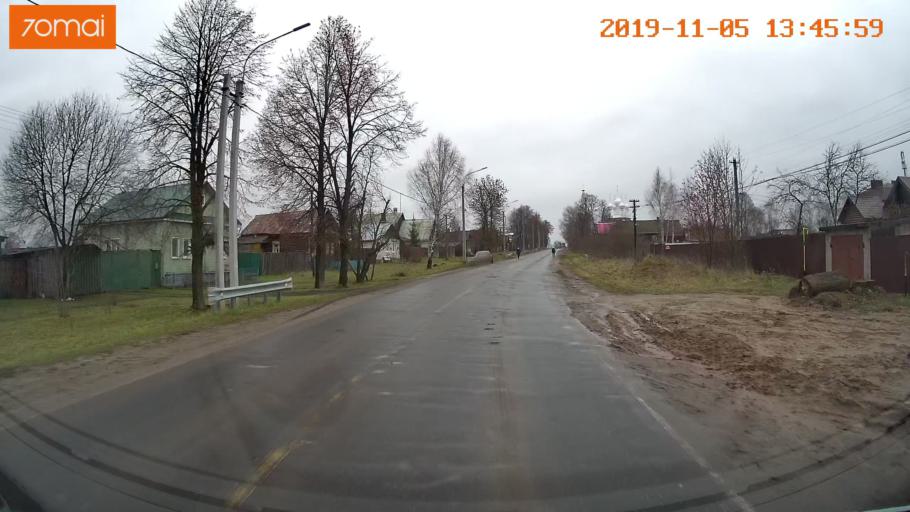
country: RU
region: Ivanovo
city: Shuya
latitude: 56.9927
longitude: 41.4103
